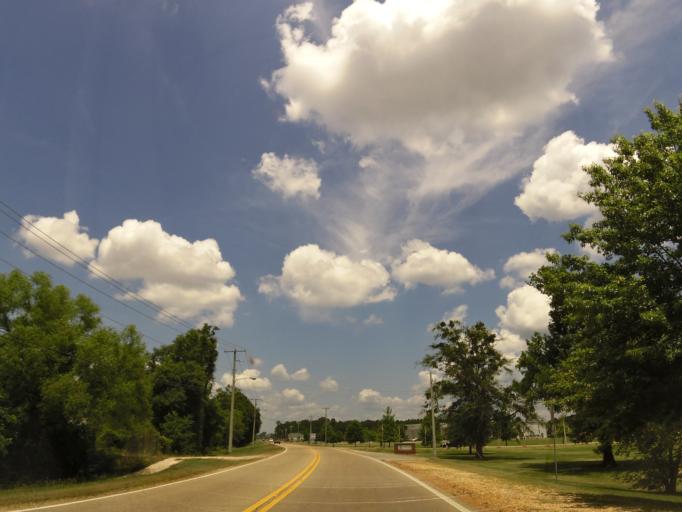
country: US
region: Mississippi
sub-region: Lee County
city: Tupelo
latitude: 34.2646
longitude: -88.6811
